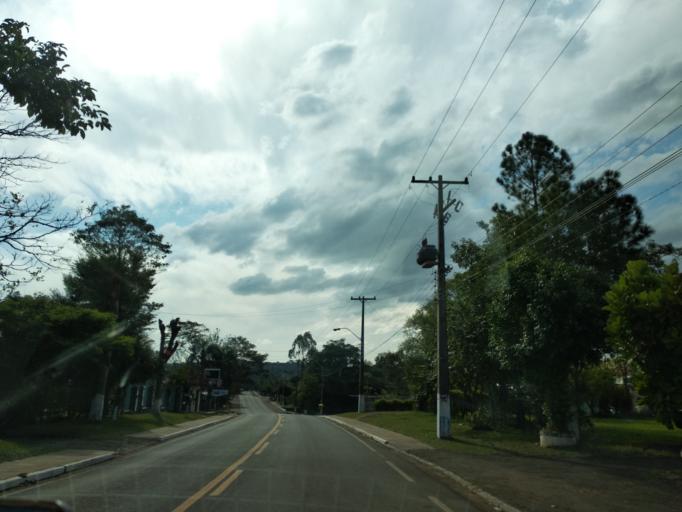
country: PY
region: Itapua
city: San Juan del Parana
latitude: -27.3018
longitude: -55.9651
